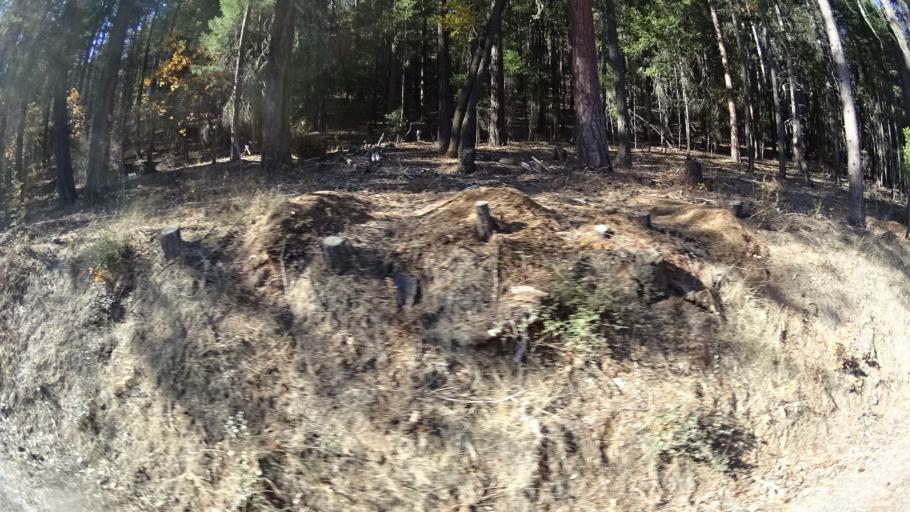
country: US
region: California
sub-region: Siskiyou County
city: Yreka
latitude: 41.8250
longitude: -122.9766
